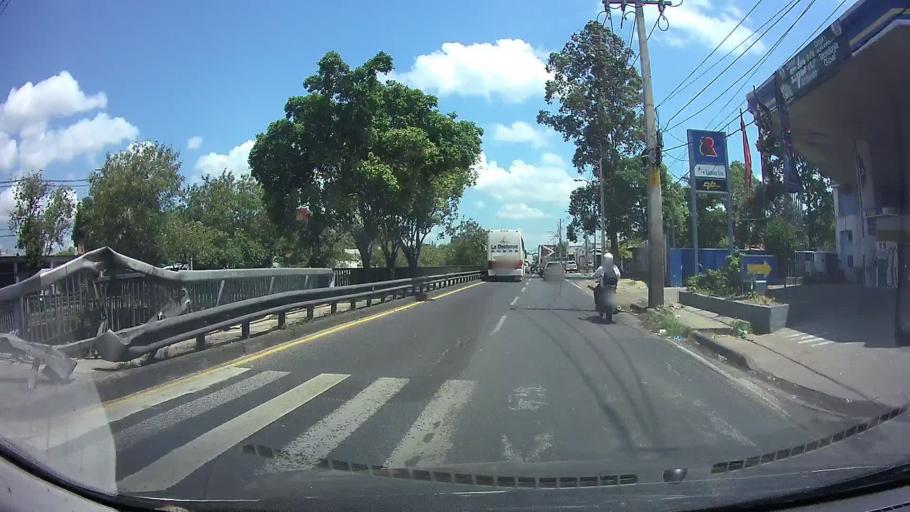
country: PY
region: Central
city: Fernando de la Mora
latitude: -25.2988
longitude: -57.5517
